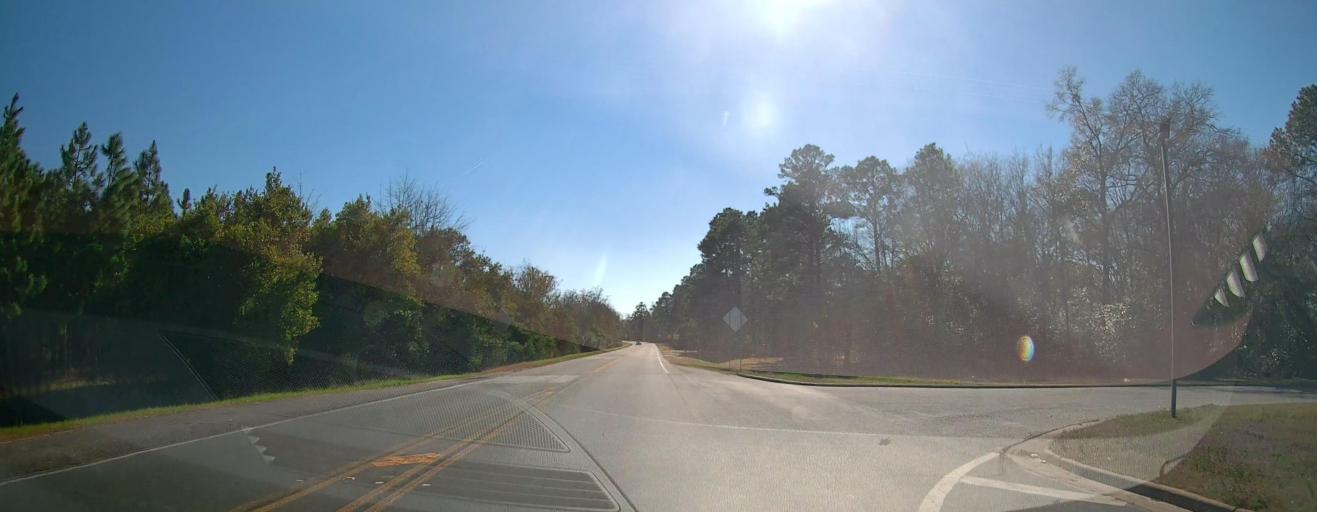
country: US
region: Georgia
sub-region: Macon County
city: Oglethorpe
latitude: 32.2683
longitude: -84.0825
